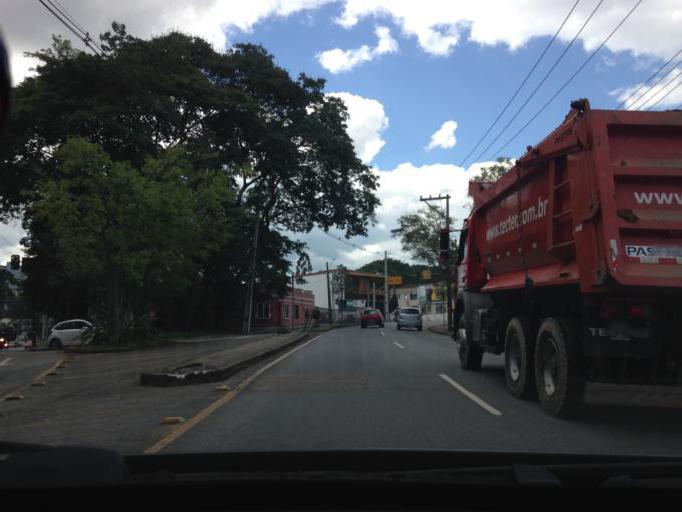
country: BR
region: Parana
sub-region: Curitiba
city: Curitiba
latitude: -25.4058
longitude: -49.2474
